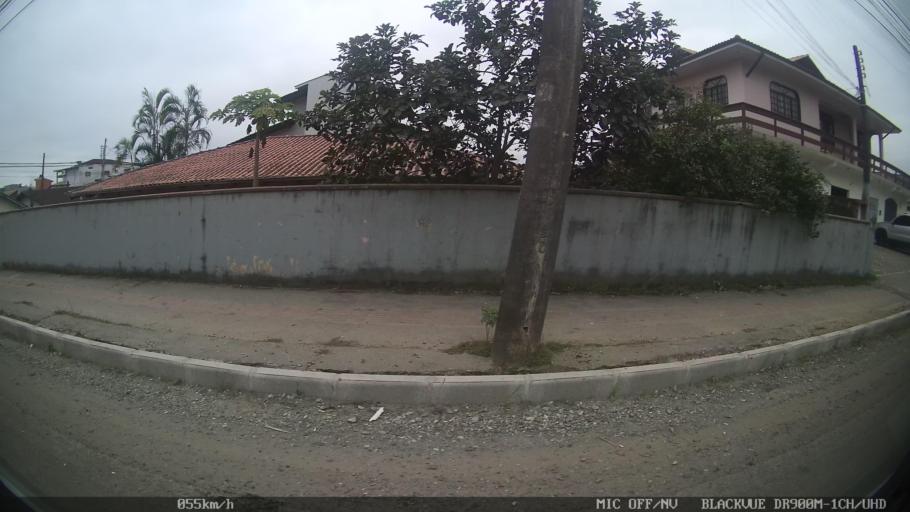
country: BR
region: Santa Catarina
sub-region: Joinville
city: Joinville
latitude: -26.2971
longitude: -48.8199
